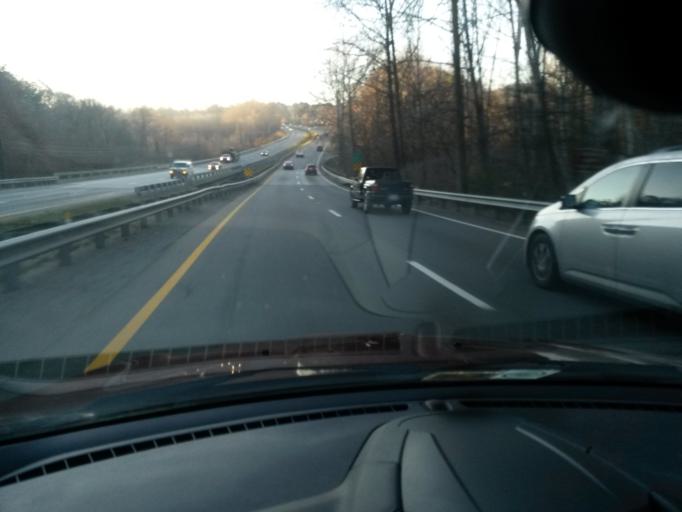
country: US
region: Virginia
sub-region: Franklin County
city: Rocky Mount
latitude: 37.0548
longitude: -79.8825
